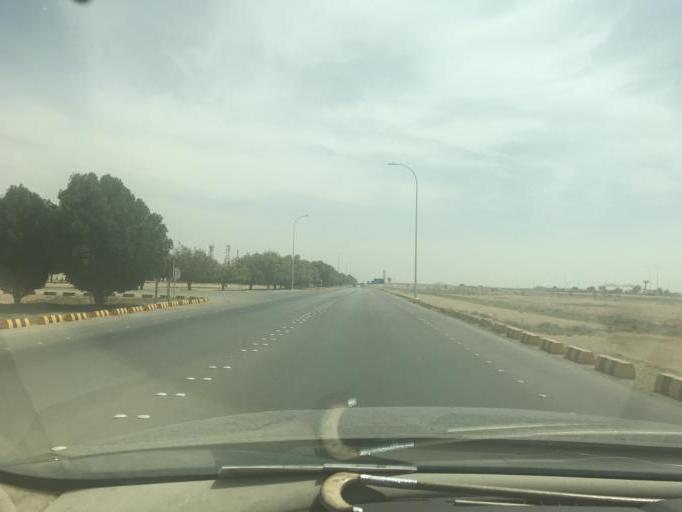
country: SA
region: Ar Riyad
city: Riyadh
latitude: 24.9822
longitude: 46.6845
